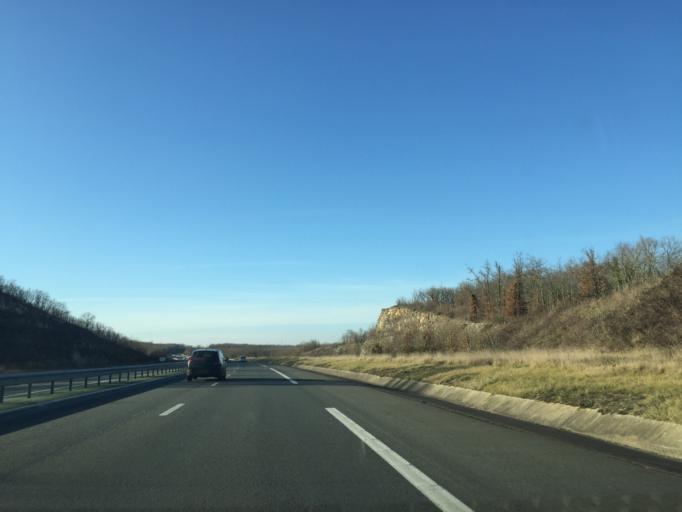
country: FR
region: Aquitaine
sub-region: Departement de la Dordogne
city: Thenon
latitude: 45.1620
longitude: 1.0531
